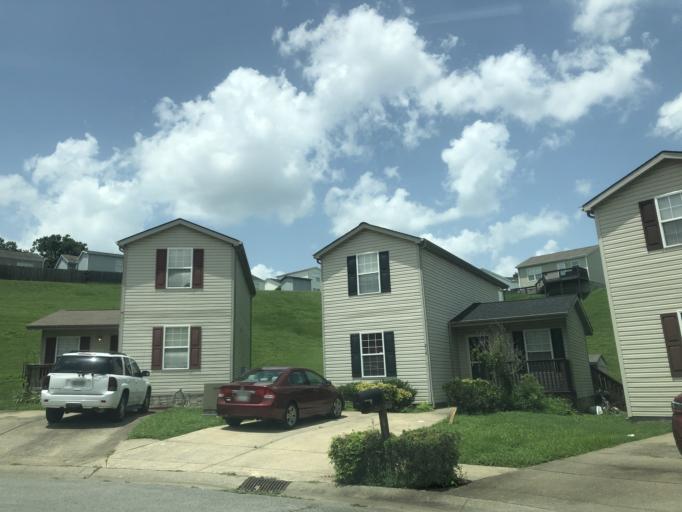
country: US
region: Tennessee
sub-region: Williamson County
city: Nolensville
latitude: 36.0496
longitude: -86.6781
